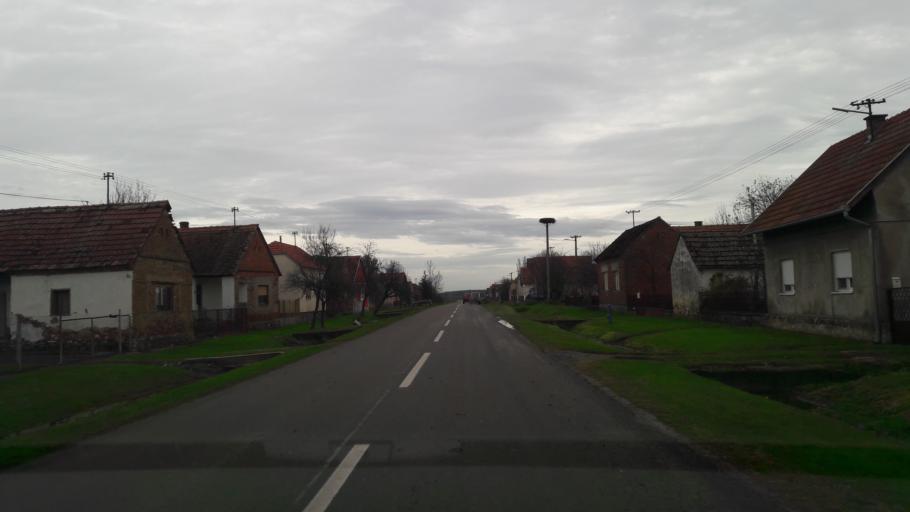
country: HR
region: Virovitick-Podravska
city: Zdenci
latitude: 45.6063
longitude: 18.0134
